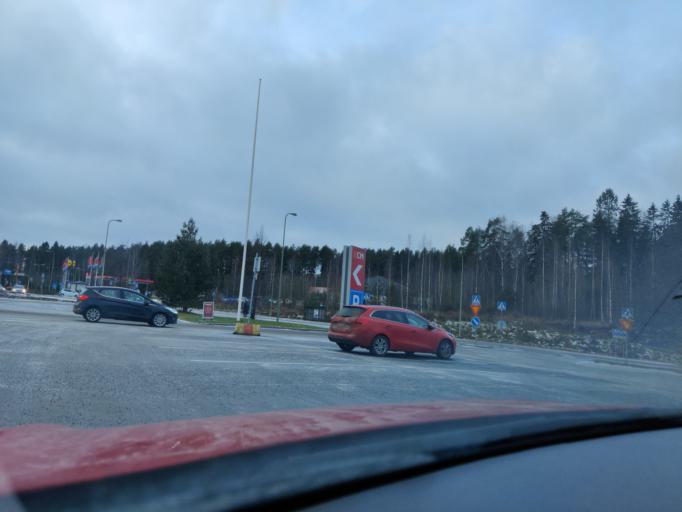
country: FI
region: Pirkanmaa
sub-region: Tampere
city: Nokia
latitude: 61.4666
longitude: 23.5084
